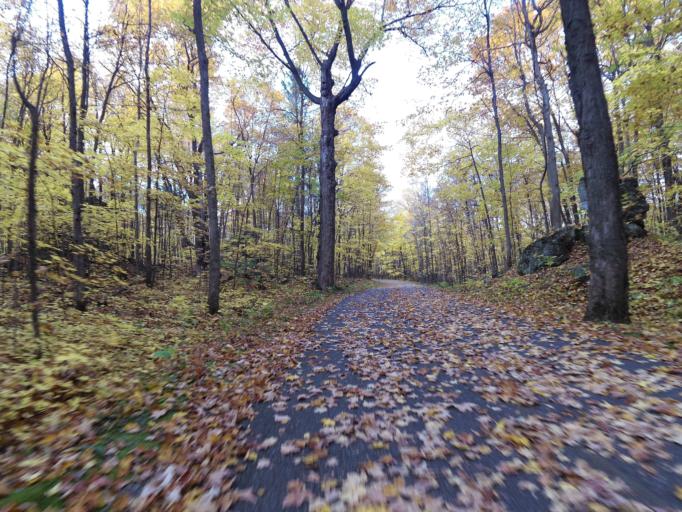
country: CA
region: Quebec
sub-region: Outaouais
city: Gatineau
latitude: 45.4599
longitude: -75.7821
